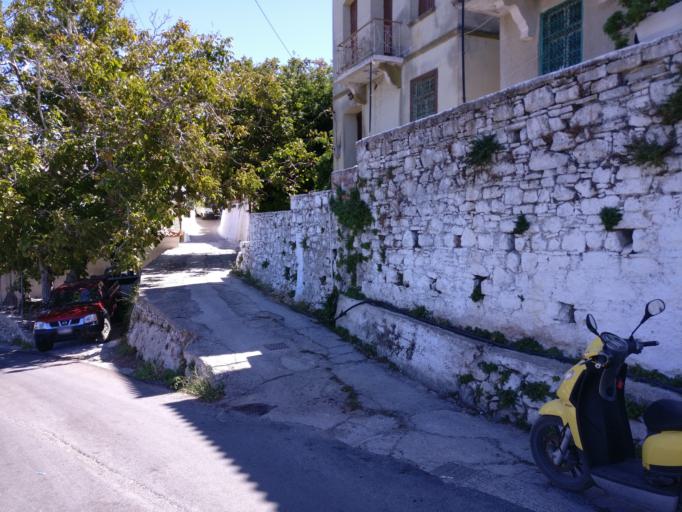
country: GR
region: North Aegean
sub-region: Nomos Samou
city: Neon Karlovasion
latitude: 37.7740
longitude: 26.6859
